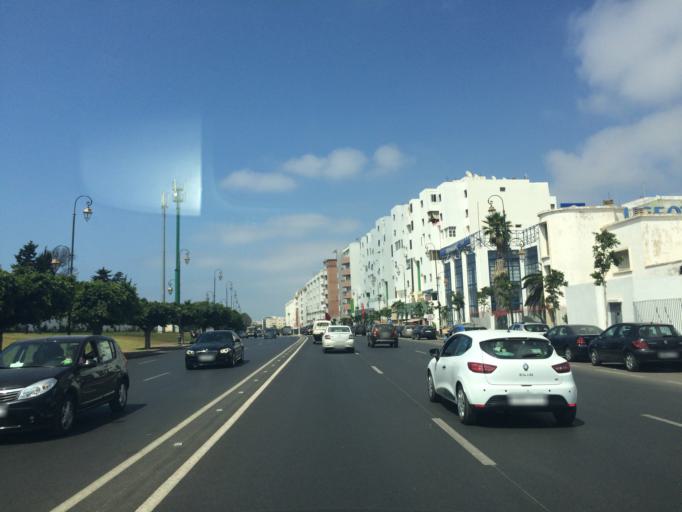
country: MA
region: Rabat-Sale-Zemmour-Zaer
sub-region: Rabat
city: Rabat
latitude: 33.9953
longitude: -6.8630
